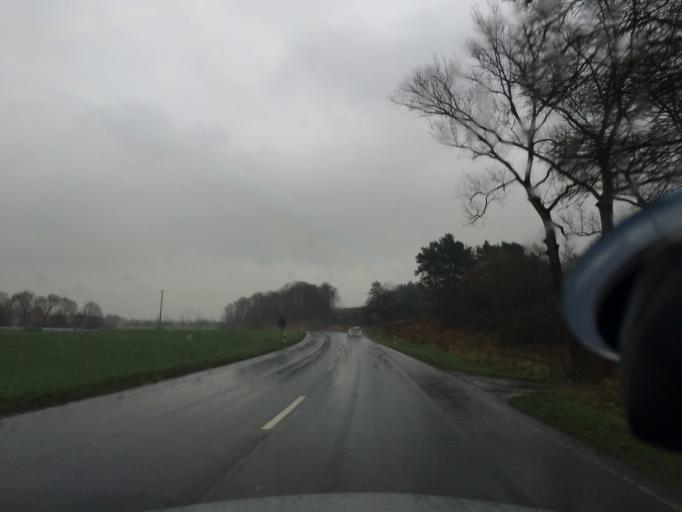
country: DE
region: Hesse
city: Staufenberg
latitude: 50.7120
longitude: 8.7697
